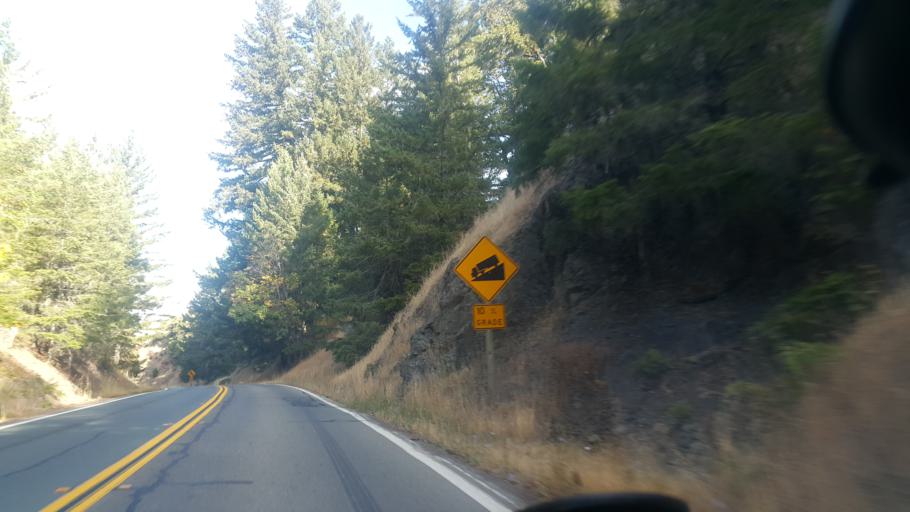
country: US
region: California
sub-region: Mendocino County
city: Brooktrails
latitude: 39.3893
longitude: -123.4432
